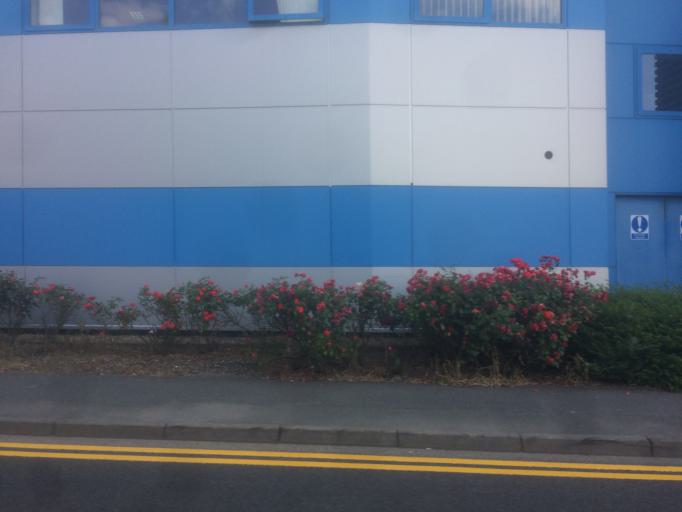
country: GB
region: England
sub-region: Luton
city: Luton
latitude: 51.8787
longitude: -0.3838
